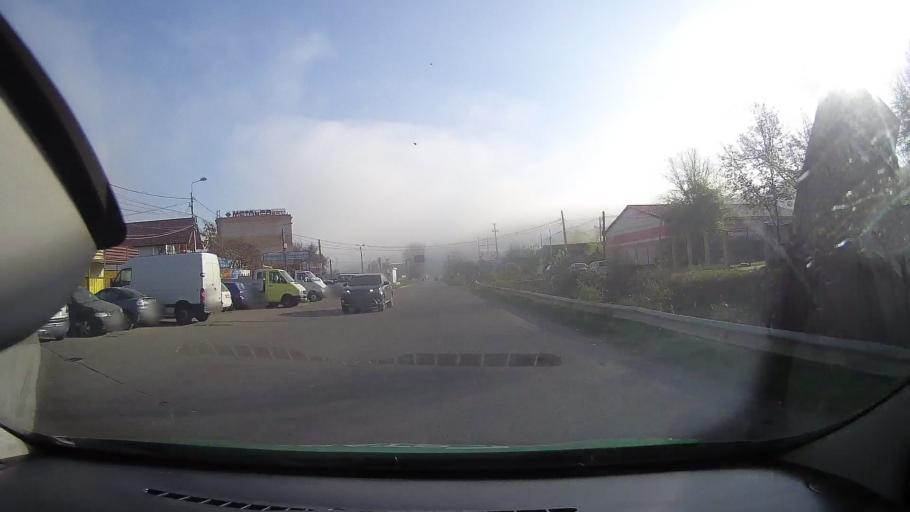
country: RO
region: Tulcea
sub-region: Municipiul Tulcea
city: Tulcea
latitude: 45.1656
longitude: 28.8201
